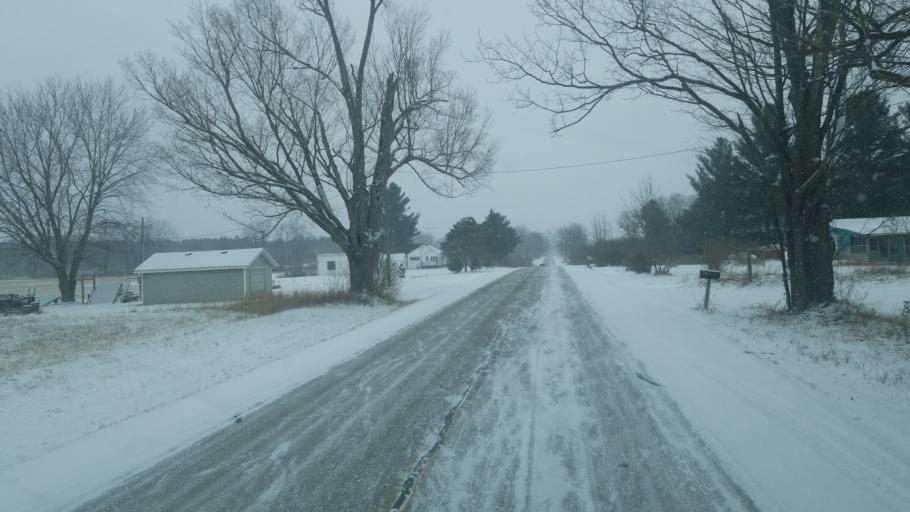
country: US
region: Michigan
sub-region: Mecosta County
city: Big Rapids
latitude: 43.7510
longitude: -85.4032
